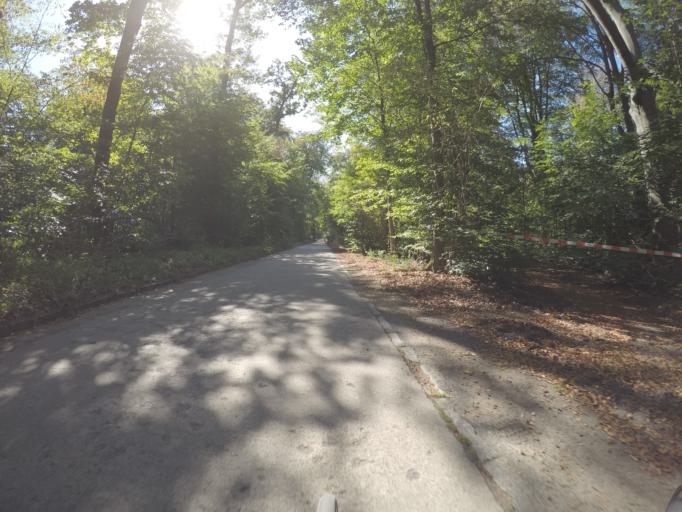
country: DE
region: Berlin
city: Heiligensee
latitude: 52.5909
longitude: 13.2567
